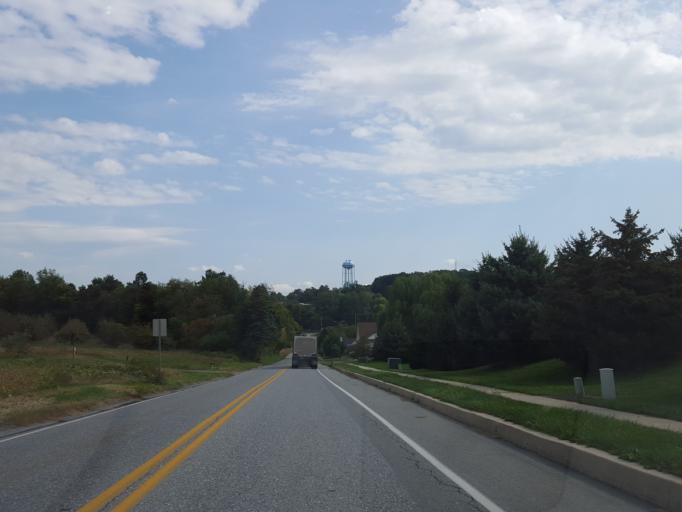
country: US
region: Pennsylvania
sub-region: York County
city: Yoe
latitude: 39.9117
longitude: -76.6519
